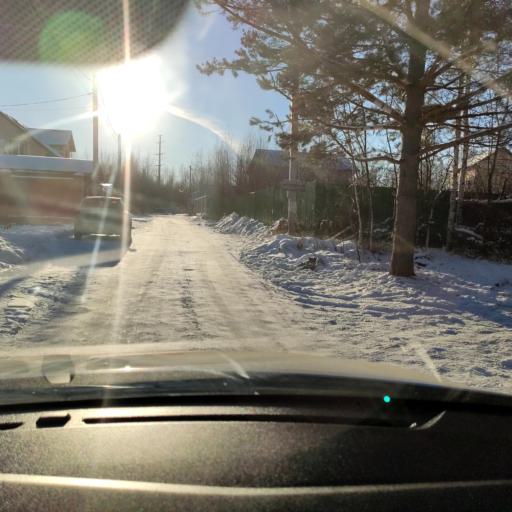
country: RU
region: Tatarstan
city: Stolbishchi
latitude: 55.7327
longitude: 49.2606
